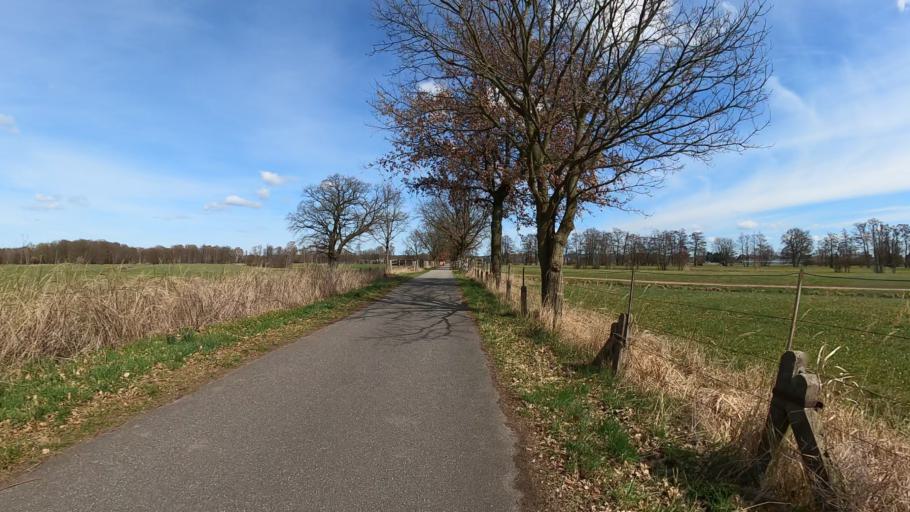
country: DE
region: Lower Saxony
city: Drage
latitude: 53.4366
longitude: 10.2927
